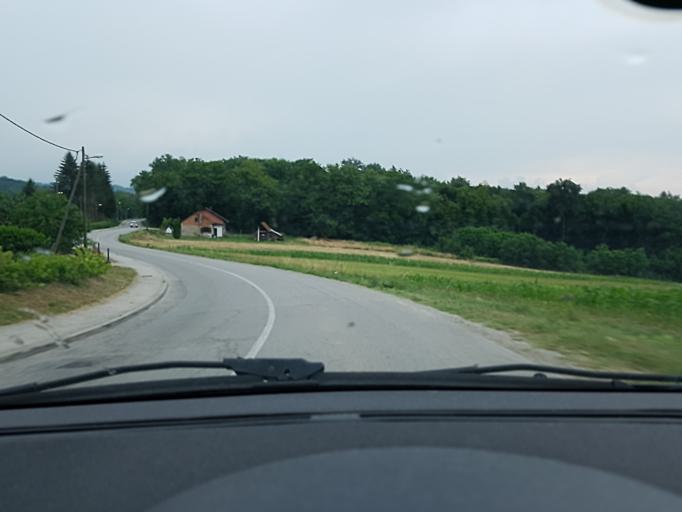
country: HR
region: Zagrebacka
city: Pojatno
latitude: 45.8942
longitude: 15.7916
